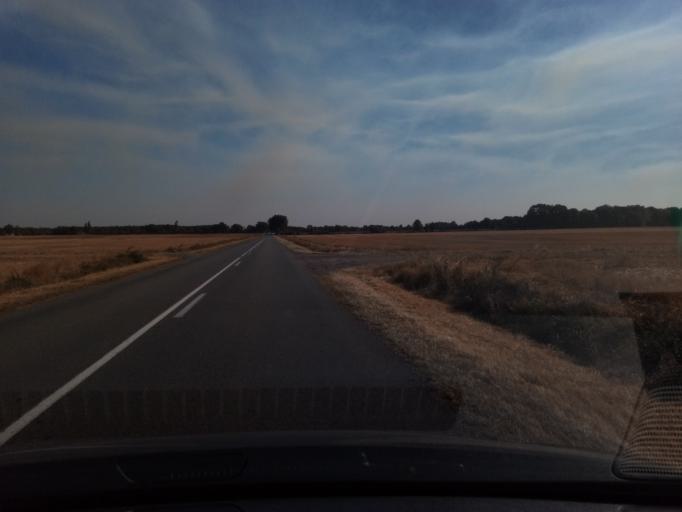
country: FR
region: Poitou-Charentes
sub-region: Departement de la Vienne
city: Montmorillon
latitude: 46.4944
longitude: 0.7826
